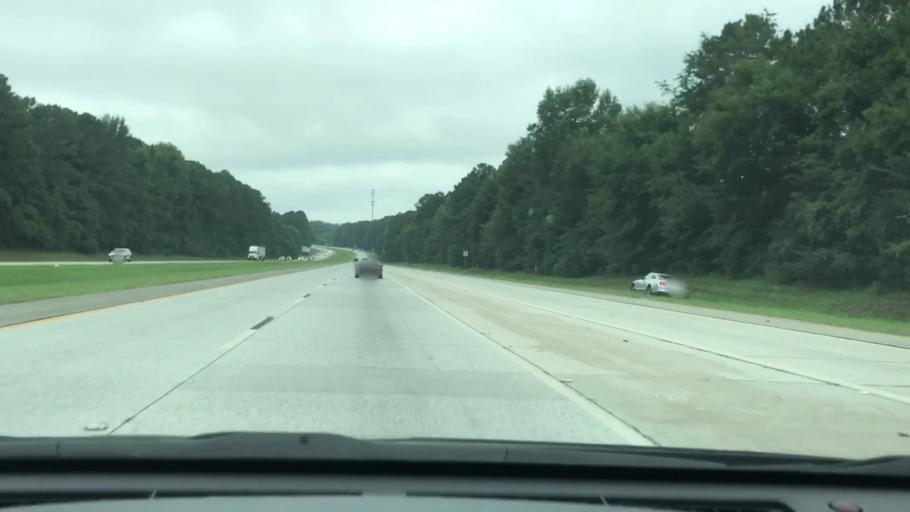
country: US
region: Georgia
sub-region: Morgan County
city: Madison
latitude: 33.5530
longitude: -83.3631
